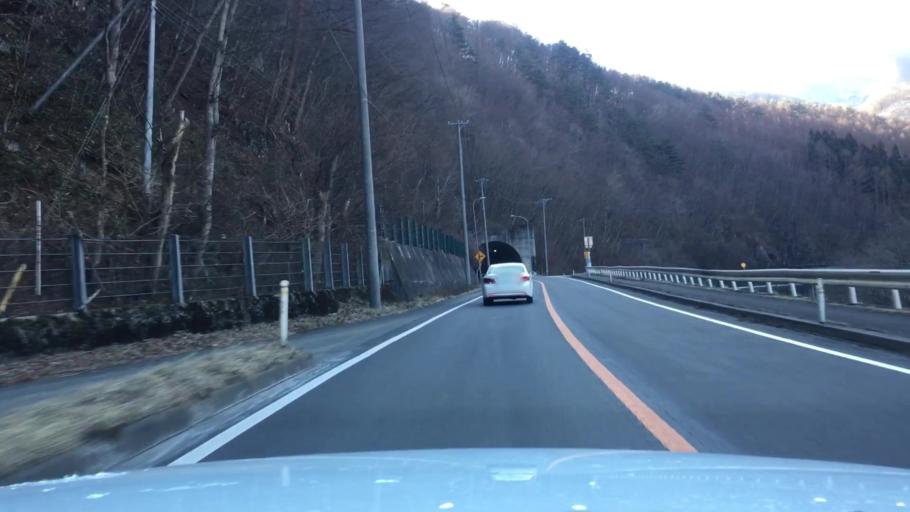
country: JP
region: Iwate
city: Tono
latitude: 39.6391
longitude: 141.6004
